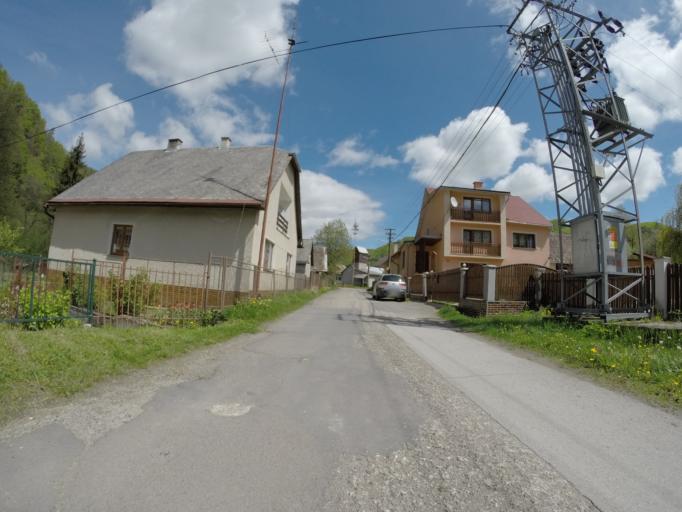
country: SK
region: Banskobystricky
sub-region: Okres Banska Bystrica
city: Banska Stiavnica
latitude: 48.5112
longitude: 18.9961
